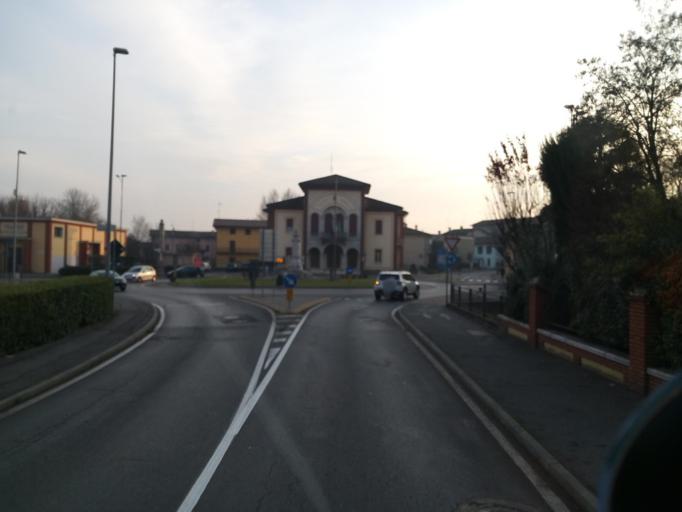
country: IT
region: Lombardy
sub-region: Provincia di Brescia
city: Poncarale
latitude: 45.4614
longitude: 10.1740
